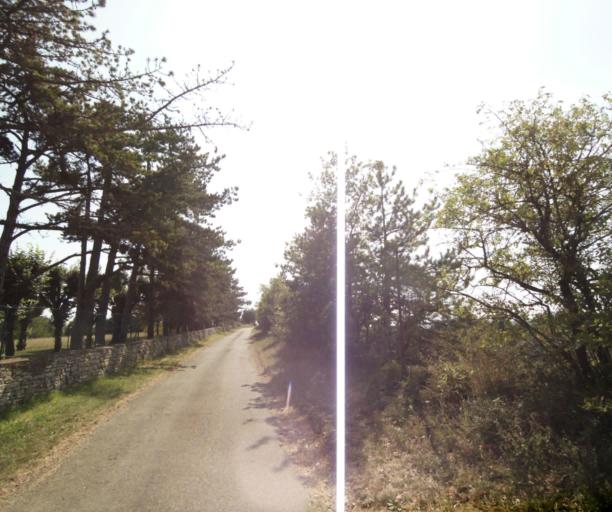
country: FR
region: Bourgogne
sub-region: Departement de Saone-et-Loire
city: Tournus
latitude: 46.5592
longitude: 4.8738
